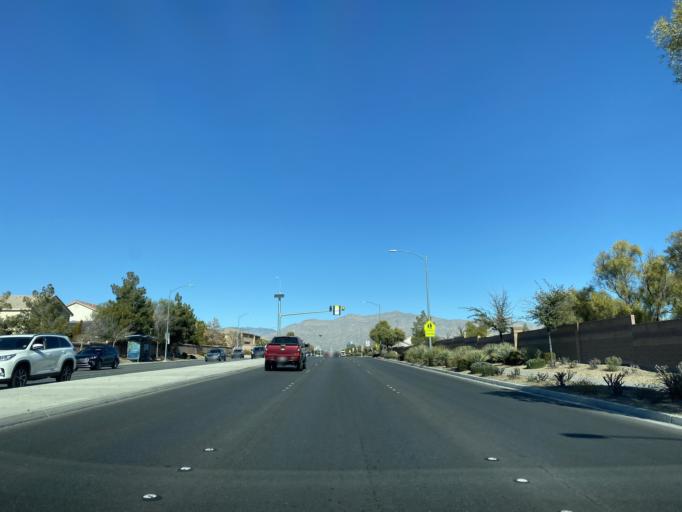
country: US
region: Nevada
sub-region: Clark County
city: North Las Vegas
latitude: 36.2640
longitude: -115.2070
